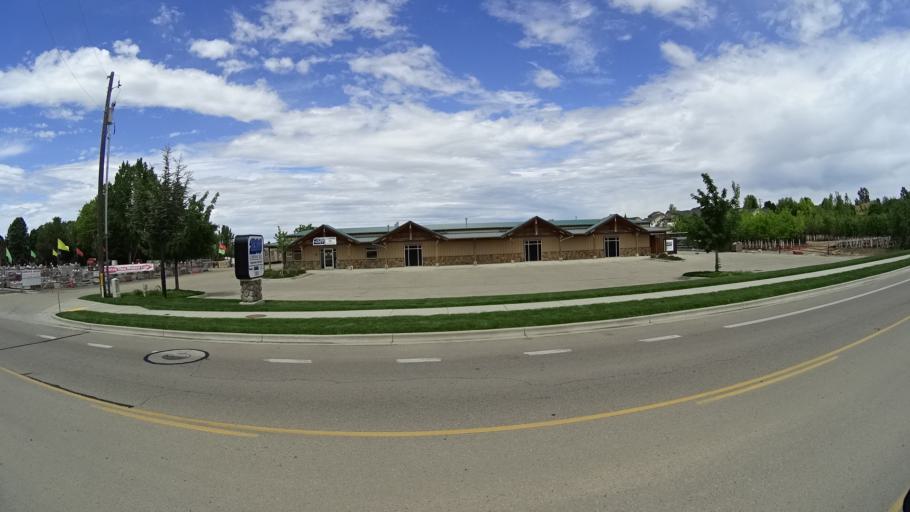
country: US
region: Idaho
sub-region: Ada County
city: Meridian
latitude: 43.5756
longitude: -116.3910
